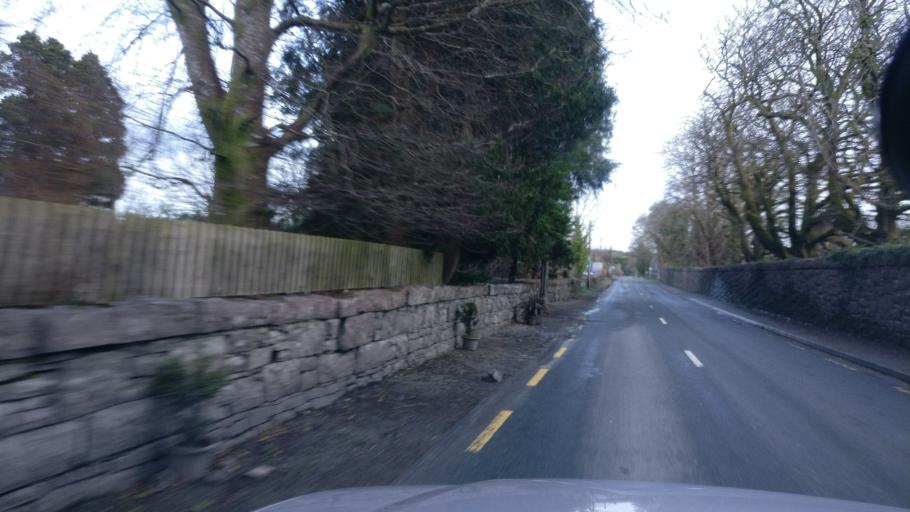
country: IE
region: Connaught
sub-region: Maigh Eo
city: Ballinrobe
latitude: 53.5422
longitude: -9.2724
